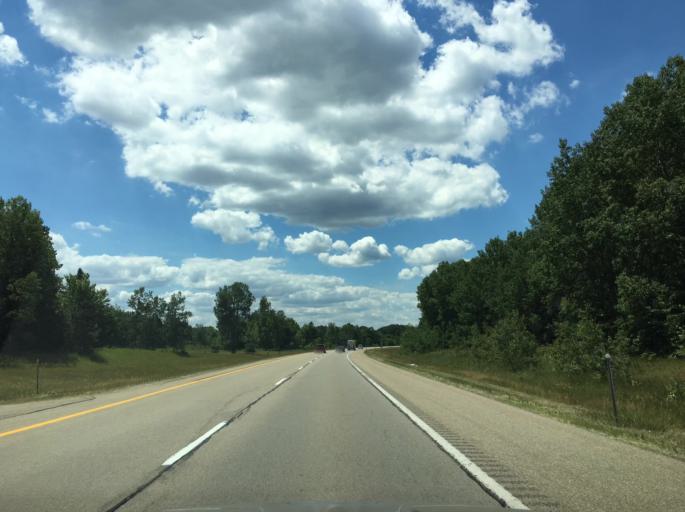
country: US
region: Michigan
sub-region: Clare County
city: Clare
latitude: 43.8779
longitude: -84.8182
